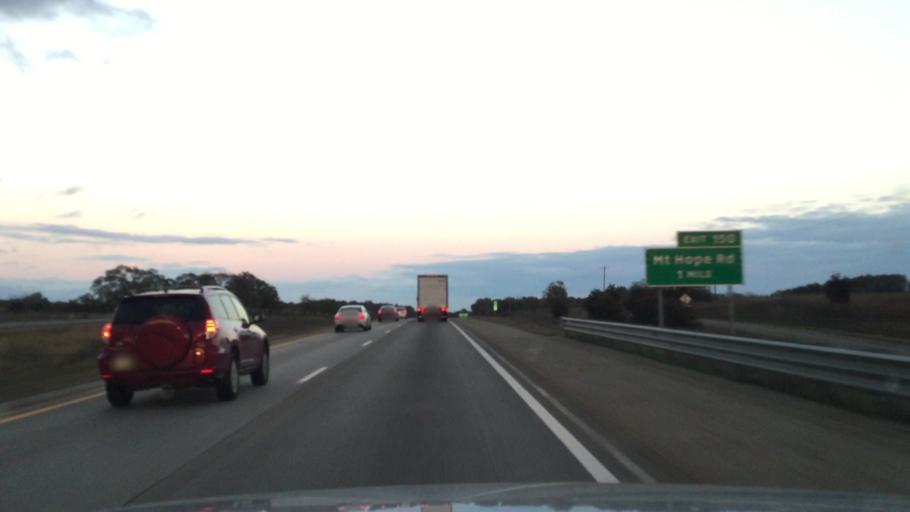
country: US
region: Michigan
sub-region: Jackson County
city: Grass Lake
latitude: 42.2921
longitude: -84.2275
